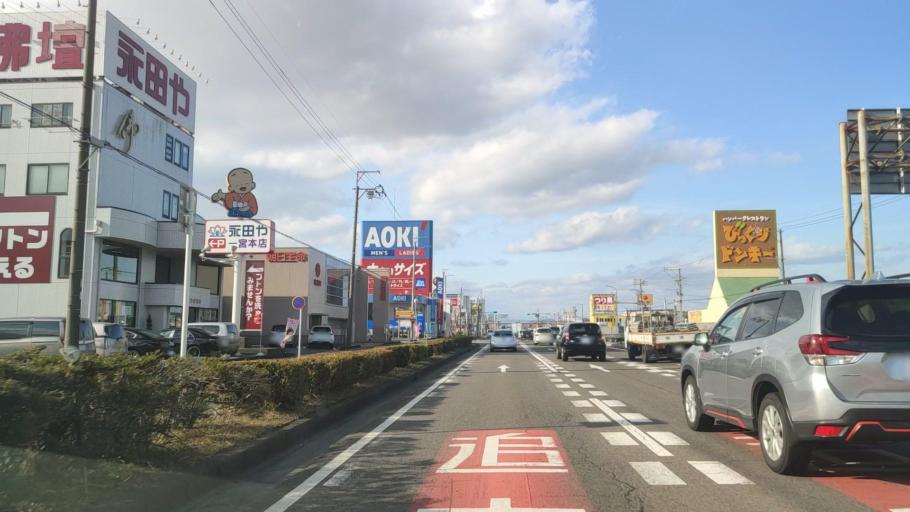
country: JP
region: Aichi
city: Ichinomiya
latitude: 35.3022
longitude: 136.8219
